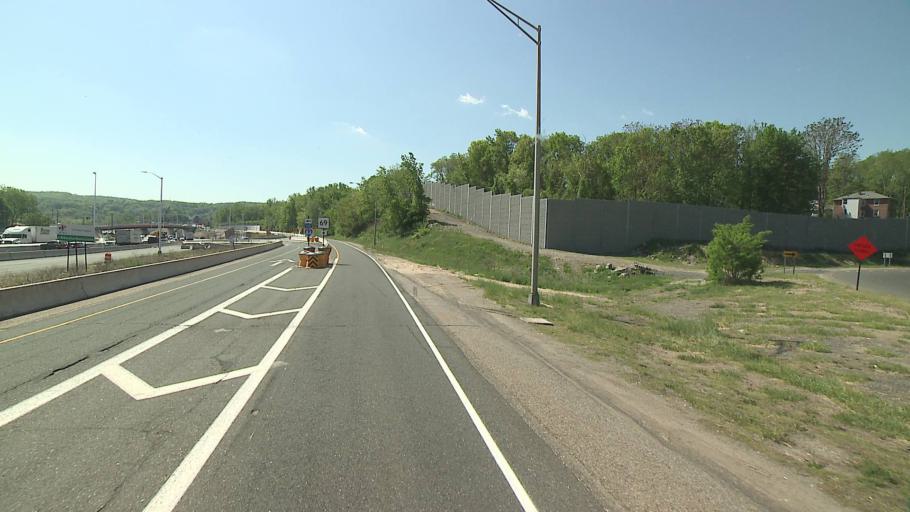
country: US
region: Connecticut
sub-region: New Haven County
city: Waterbury
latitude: 41.5445
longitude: -73.0265
